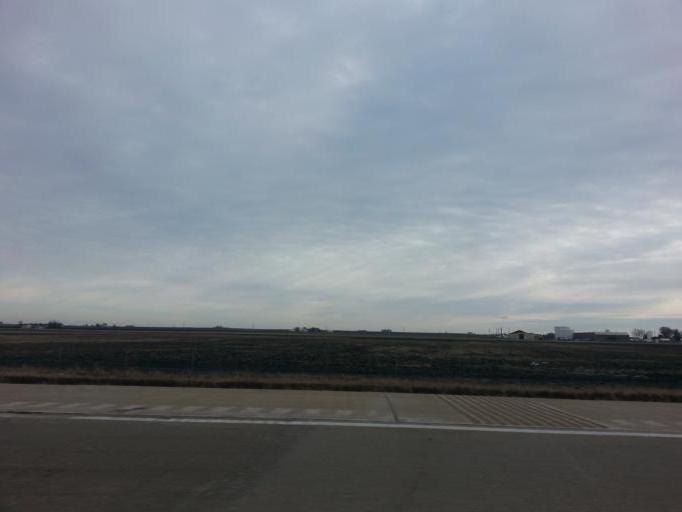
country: US
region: Illinois
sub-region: Woodford County
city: El Paso
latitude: 40.7096
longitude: -89.0296
